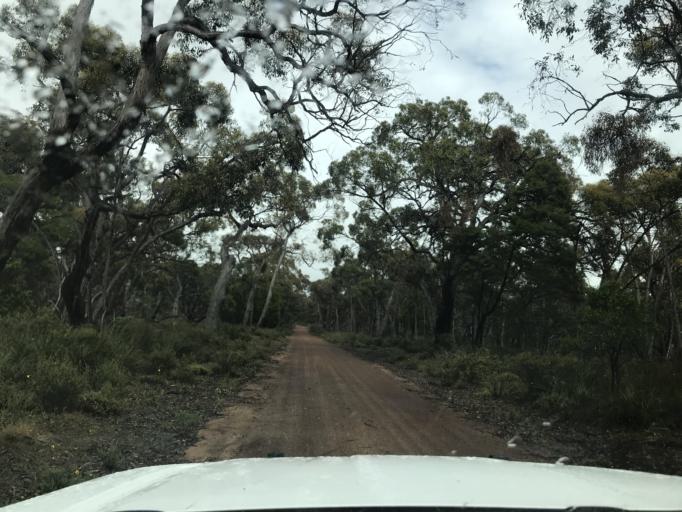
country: AU
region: South Australia
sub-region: Wattle Range
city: Penola
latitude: -37.2594
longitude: 141.3357
